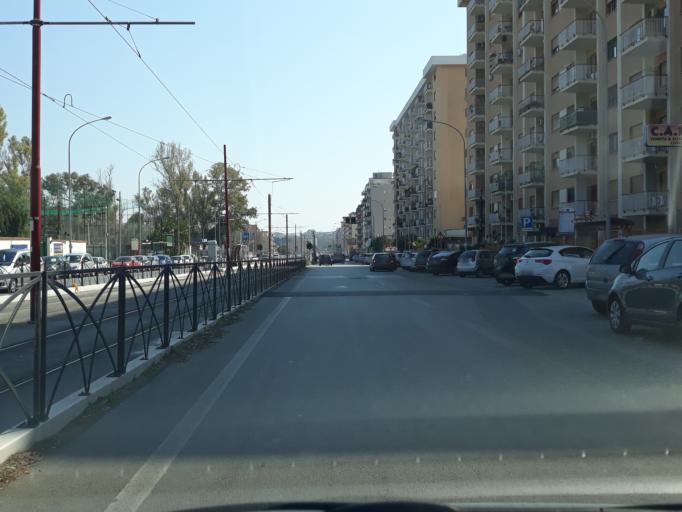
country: IT
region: Sicily
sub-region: Palermo
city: Palermo
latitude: 38.1266
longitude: 13.3087
